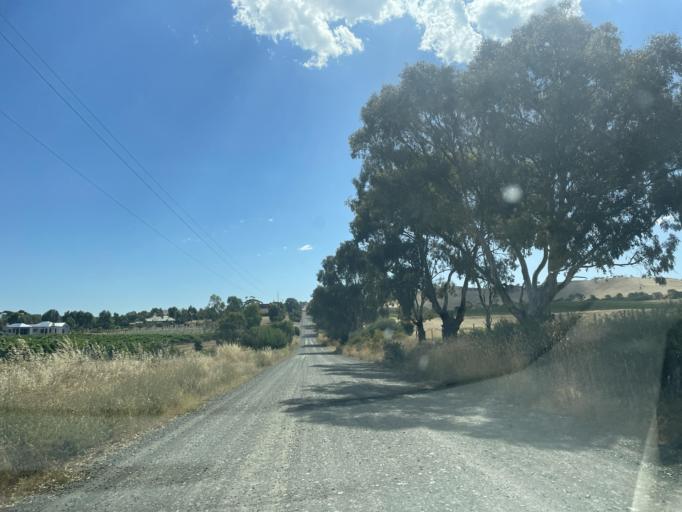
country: AU
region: South Australia
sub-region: Clare and Gilbert Valleys
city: Clare
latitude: -33.9113
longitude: 138.7237
